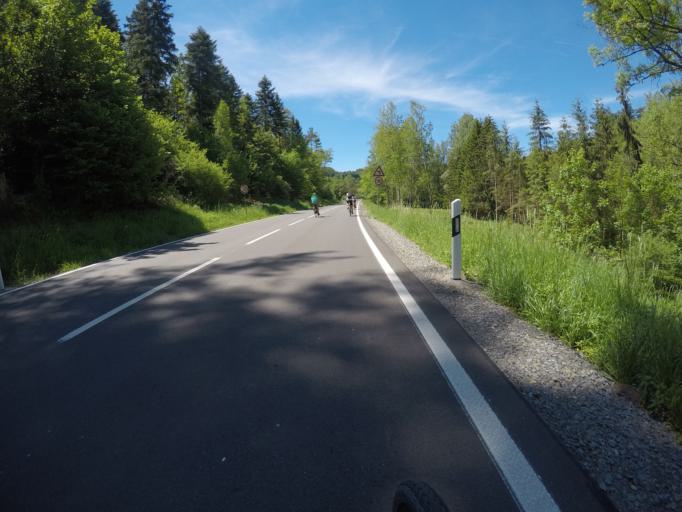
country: DE
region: Baden-Wuerttemberg
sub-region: Karlsruhe Region
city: Tiefenbronn
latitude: 48.8096
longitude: 8.8066
